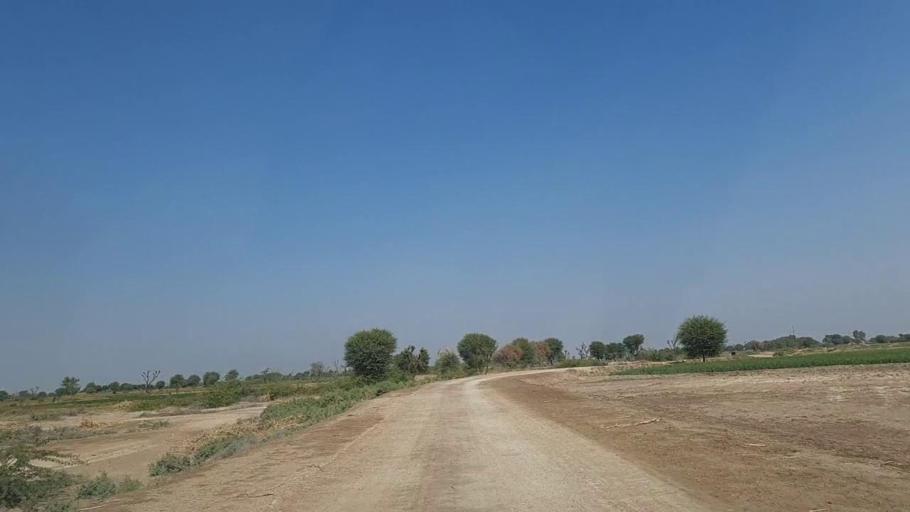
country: PK
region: Sindh
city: Digri
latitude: 25.1999
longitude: 69.1397
